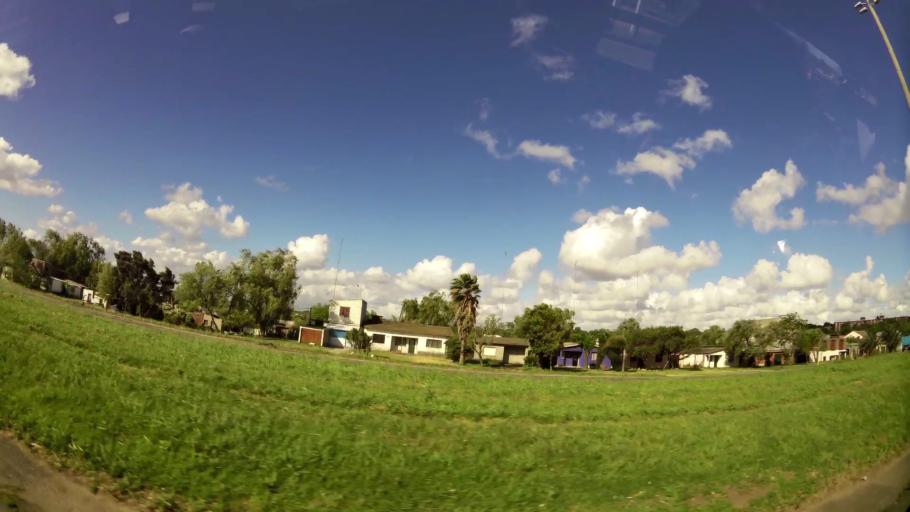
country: UY
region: Montevideo
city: Montevideo
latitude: -34.8672
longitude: -56.2461
